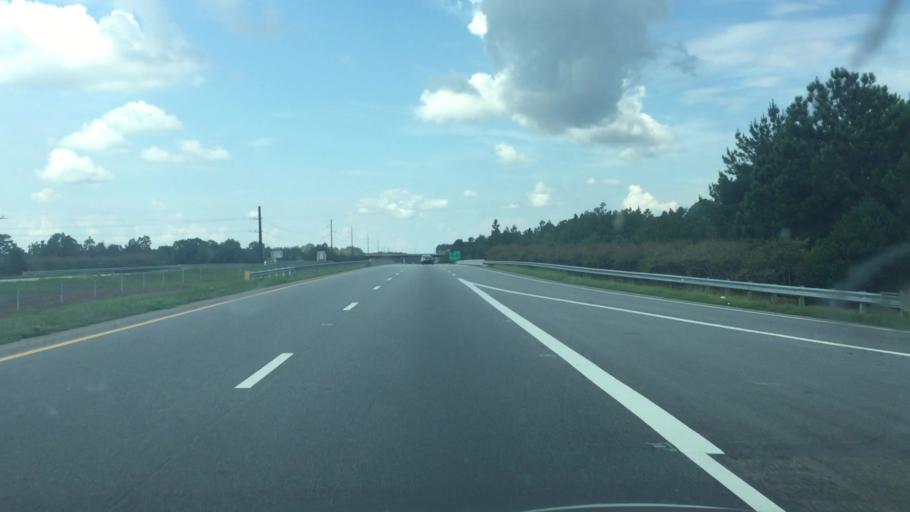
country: US
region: North Carolina
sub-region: Richmond County
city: Hamlet
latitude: 34.8642
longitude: -79.6706
